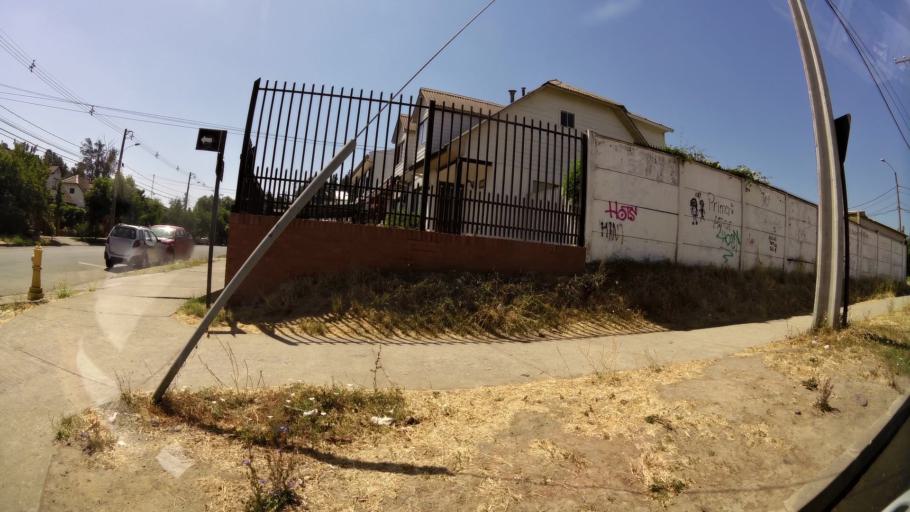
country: CL
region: Maule
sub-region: Provincia de Talca
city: Talca
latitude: -35.4243
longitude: -71.6249
